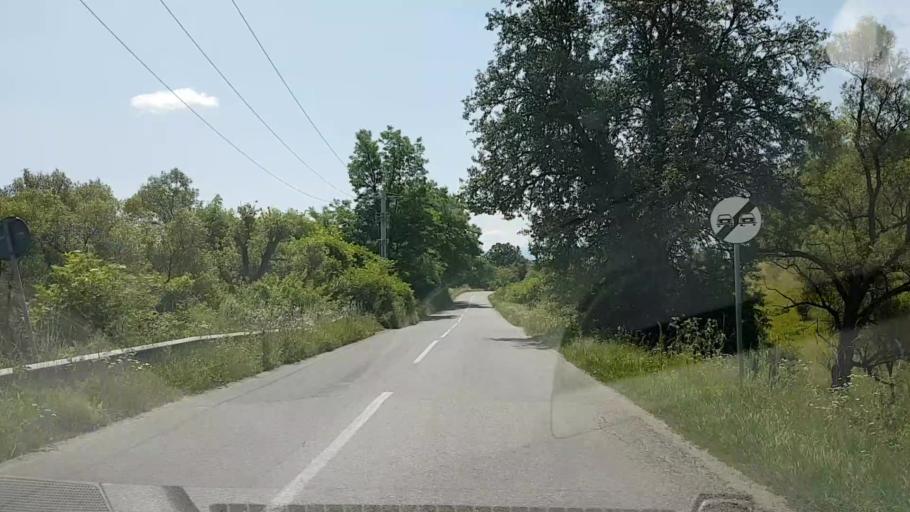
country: RO
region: Brasov
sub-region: Comuna Voila
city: Voila
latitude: 45.8679
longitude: 24.8236
